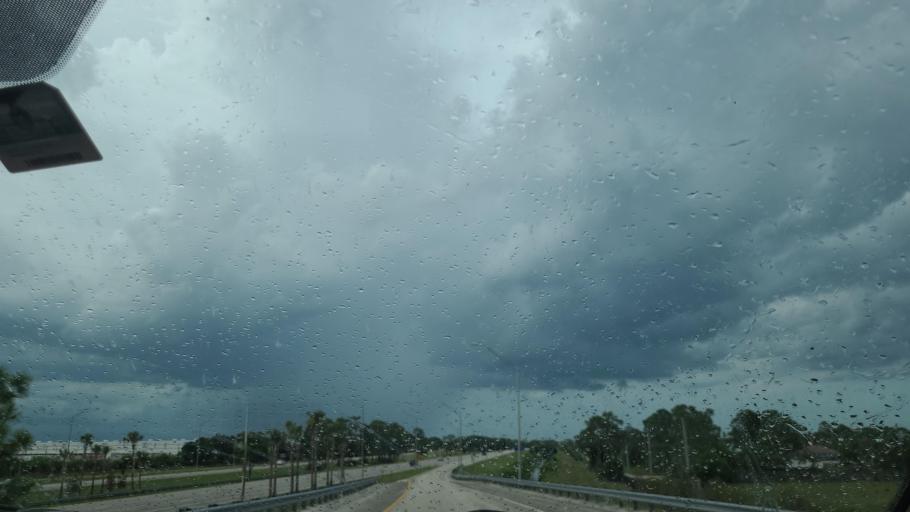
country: US
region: Florida
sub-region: Saint Lucie County
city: Port Saint Lucie
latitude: 27.2102
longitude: -80.3997
